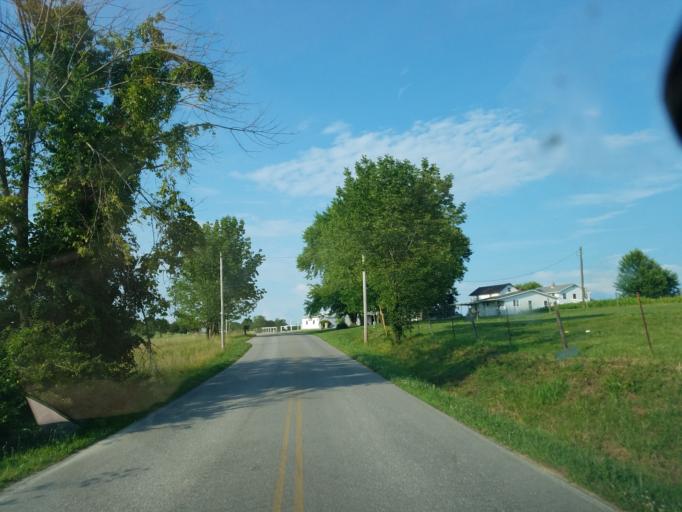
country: US
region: Ohio
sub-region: Adams County
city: West Union
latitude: 38.9032
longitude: -83.5185
